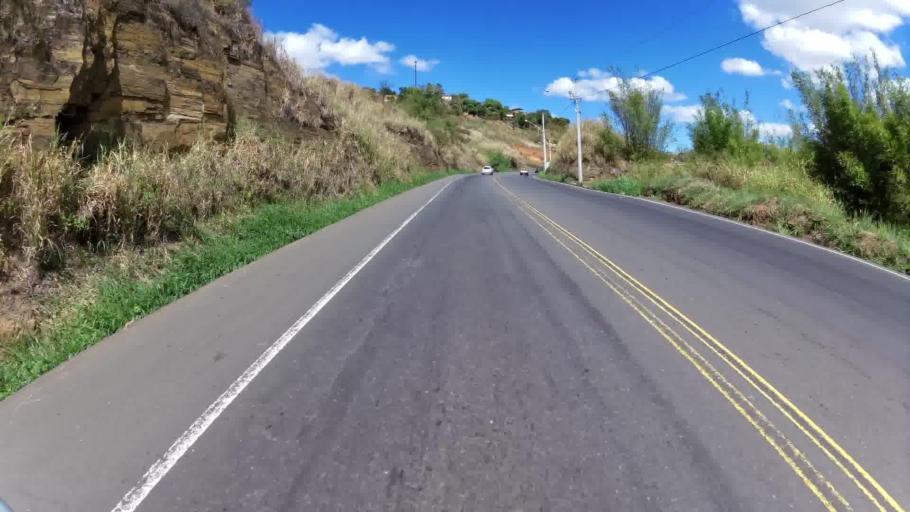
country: BR
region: Minas Gerais
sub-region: Alem Paraiba
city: Alem Paraiba
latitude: -21.8615
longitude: -42.6674
